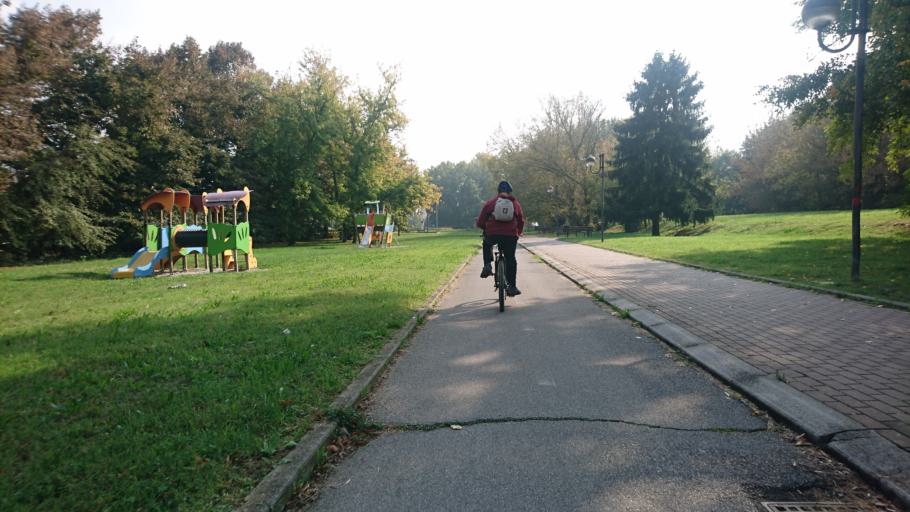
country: IT
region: Veneto
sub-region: Provincia di Rovigo
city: Rovigo
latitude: 45.0705
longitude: 11.7820
